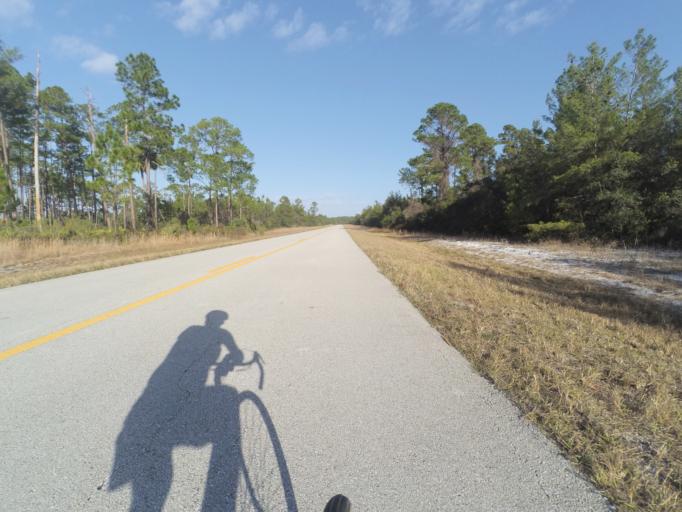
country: US
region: Florida
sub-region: Lake County
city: Astor
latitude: 29.1211
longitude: -81.5767
